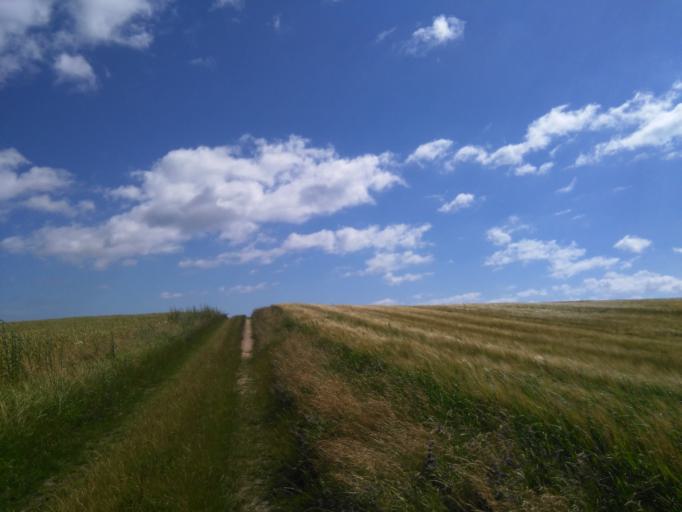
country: DK
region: Central Jutland
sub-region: Syddjurs Kommune
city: Ronde
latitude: 56.1672
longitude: 10.4186
